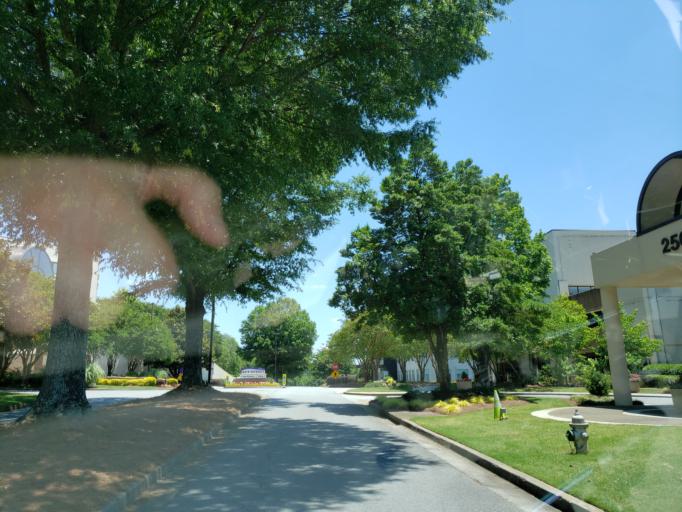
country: US
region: Georgia
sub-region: Fulton County
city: Alpharetta
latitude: 34.0627
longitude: -84.3212
